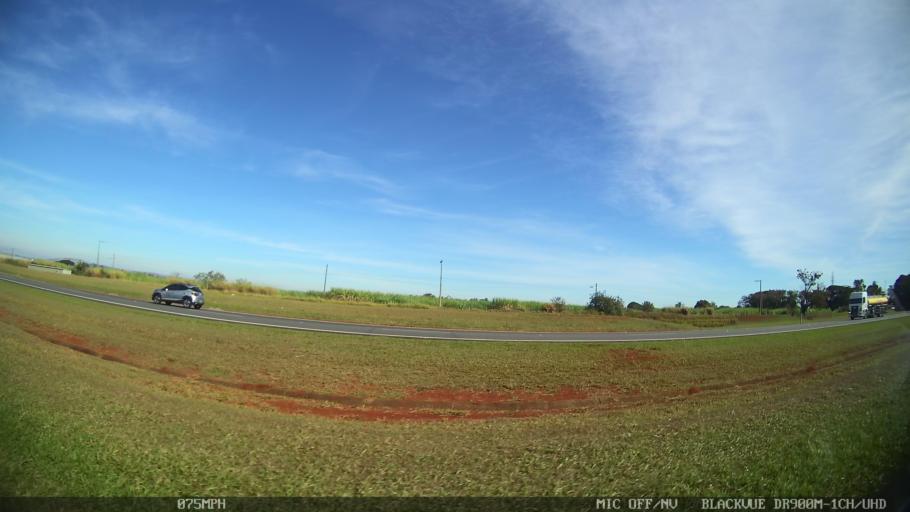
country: BR
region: Sao Paulo
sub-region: Cordeiropolis
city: Cordeiropolis
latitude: -22.4640
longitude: -47.3990
